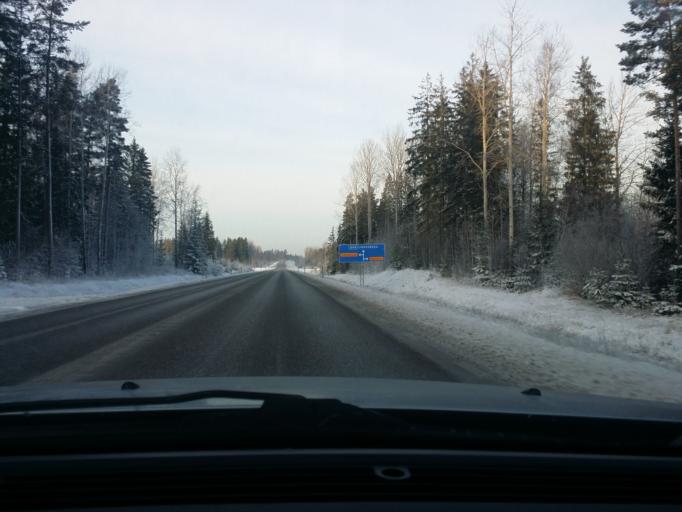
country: SE
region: OErebro
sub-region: Lindesbergs Kommun
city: Frovi
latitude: 59.4653
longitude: 15.4197
